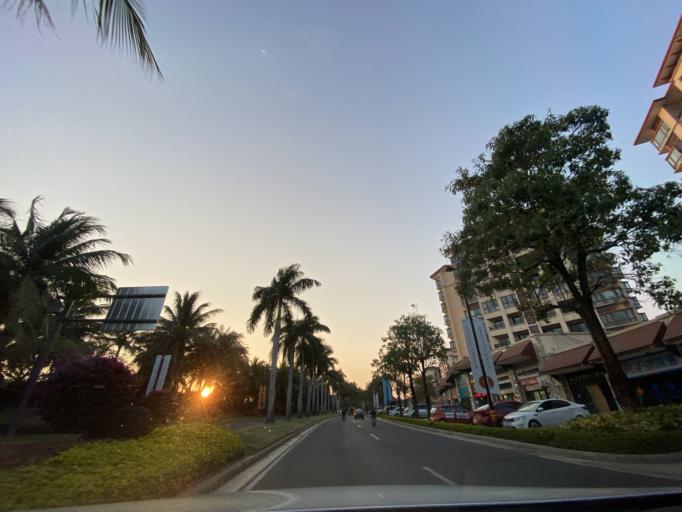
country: CN
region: Hainan
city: Yingzhou
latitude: 18.3969
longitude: 109.8550
